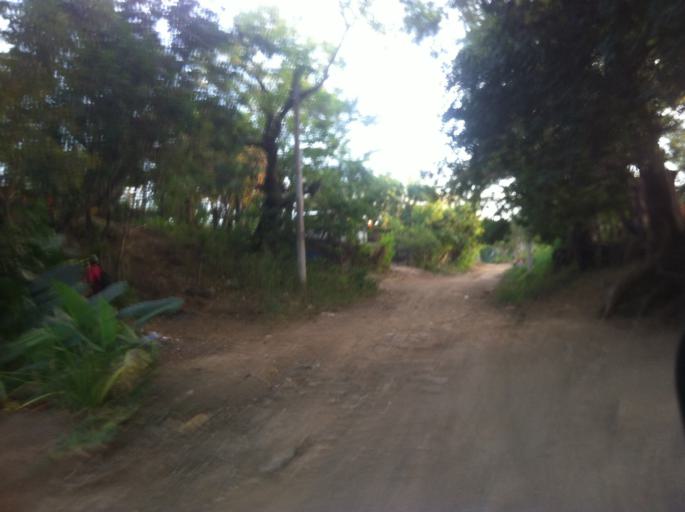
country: NI
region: Managua
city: Ciudad Sandino
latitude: 12.0985
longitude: -86.3332
